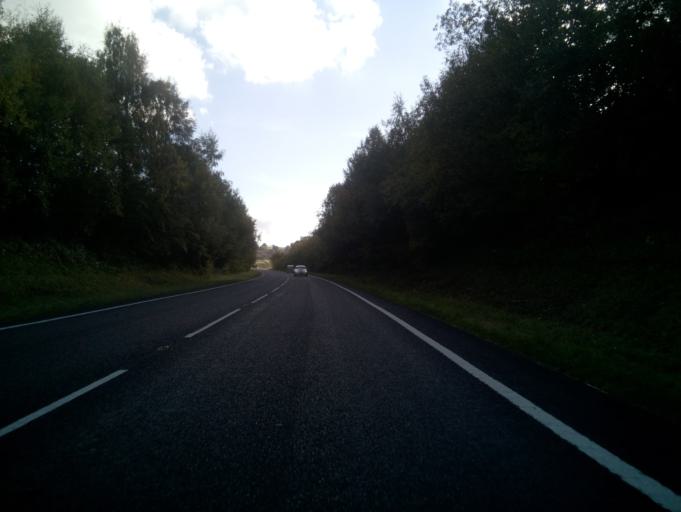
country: GB
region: Wales
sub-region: Sir Powys
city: Brecon
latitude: 51.9840
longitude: -3.3289
